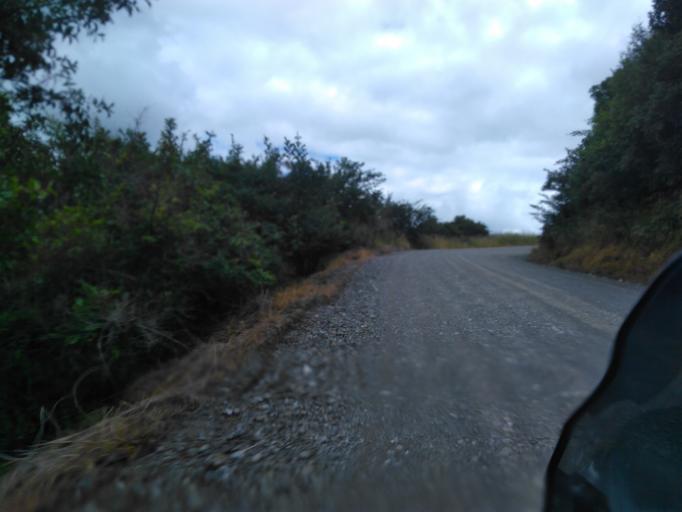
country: NZ
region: Gisborne
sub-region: Gisborne District
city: Gisborne
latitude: -38.1542
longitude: 178.1313
